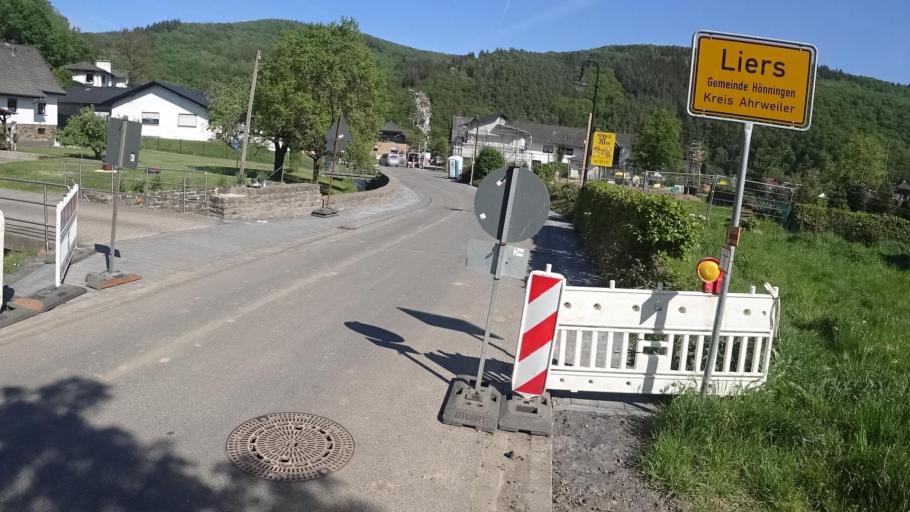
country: DE
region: Rheinland-Pfalz
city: Honningen
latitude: 50.4586
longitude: 6.9415
